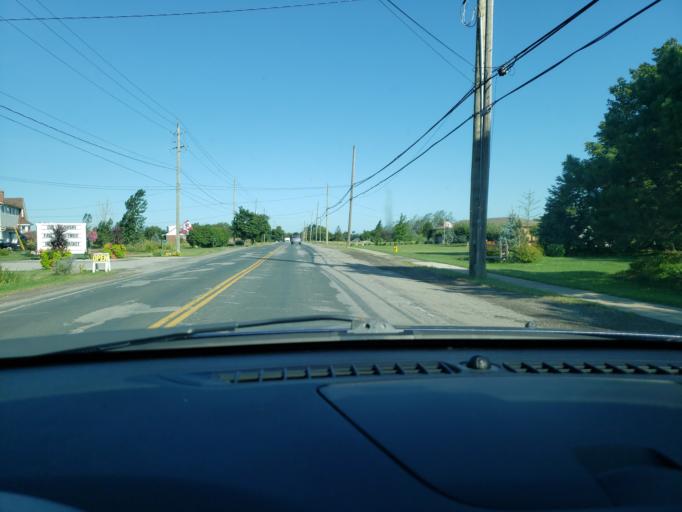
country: CA
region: Ontario
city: Hamilton
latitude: 43.2017
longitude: -79.6110
